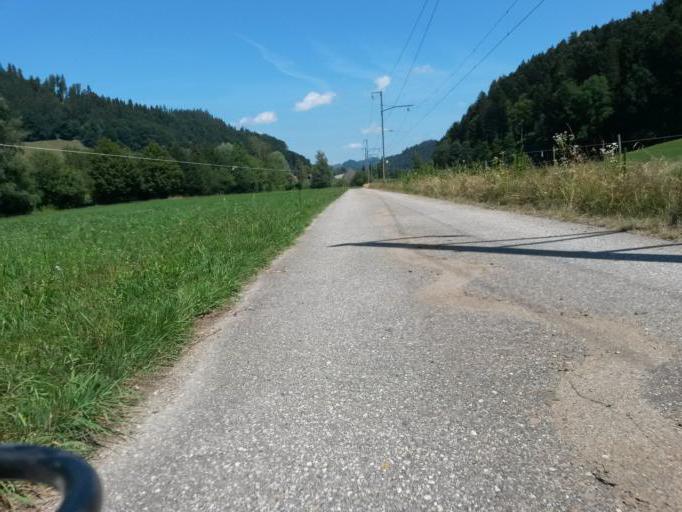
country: CH
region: Bern
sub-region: Bern-Mittelland District
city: Walkringen
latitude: 46.9794
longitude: 7.6407
